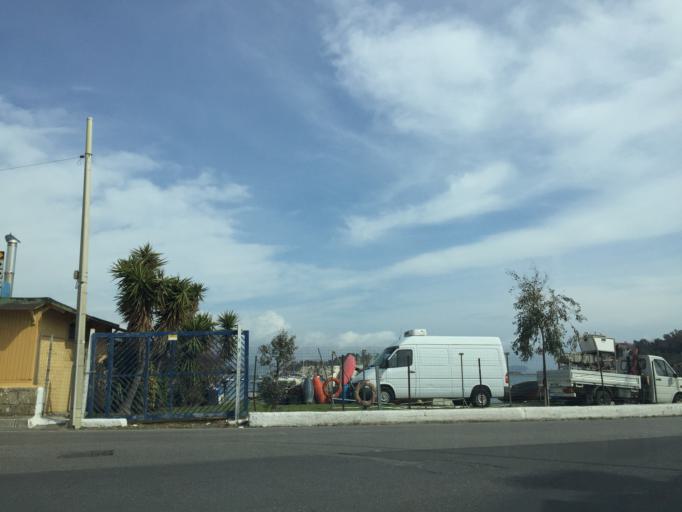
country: IT
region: Campania
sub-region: Provincia di Napoli
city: Bacoli
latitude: 40.7897
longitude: 14.0775
